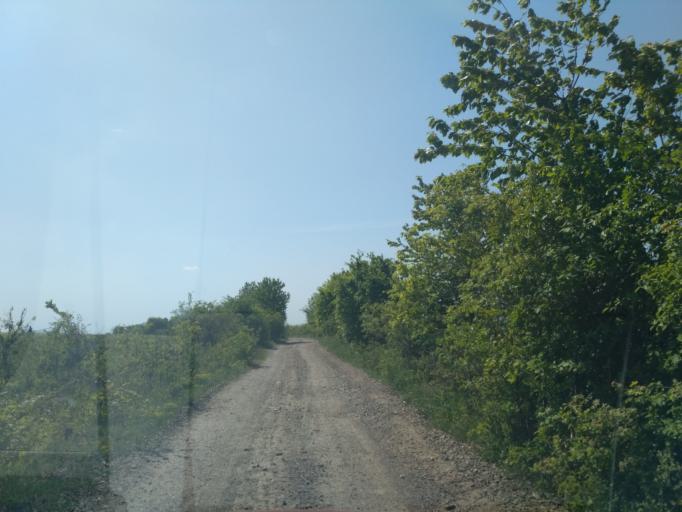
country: SK
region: Kosicky
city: Kosice
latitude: 48.8329
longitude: 21.4511
